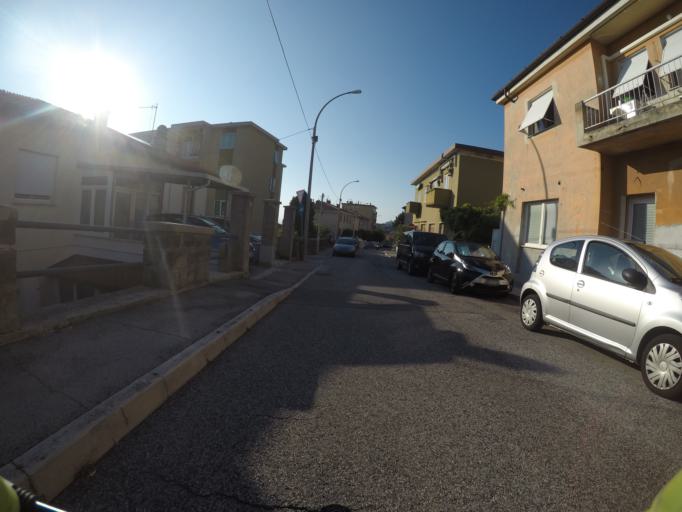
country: IT
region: Friuli Venezia Giulia
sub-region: Provincia di Trieste
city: Trieste
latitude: 45.6477
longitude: 13.7952
